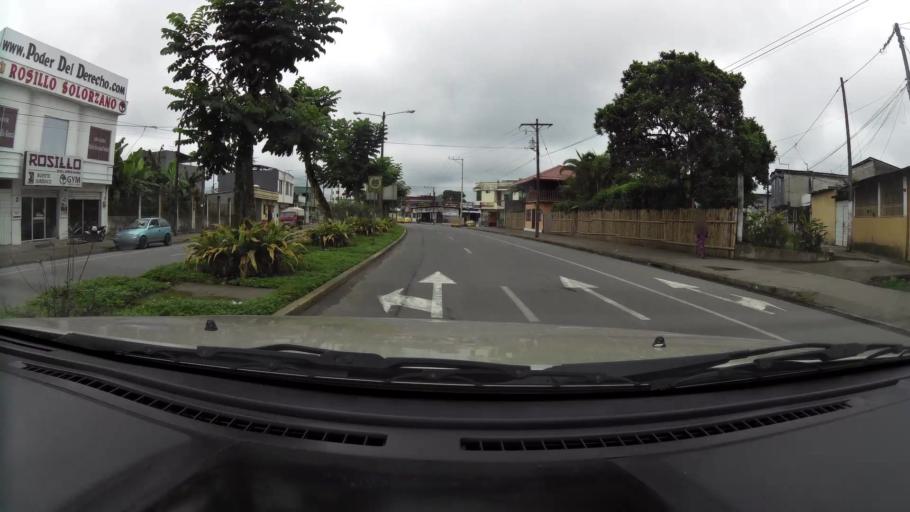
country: EC
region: Santo Domingo de los Tsachilas
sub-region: Canton Santo Domingo de los Colorados
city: Santo Domingo de los Colorados
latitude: -0.2648
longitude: -79.1774
